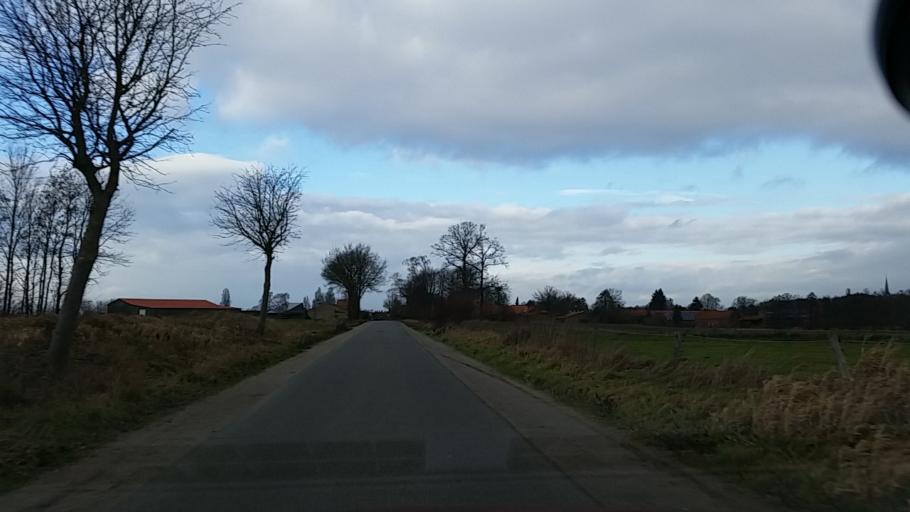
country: DE
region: Lower Saxony
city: Wieren
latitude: 52.8782
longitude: 10.6552
